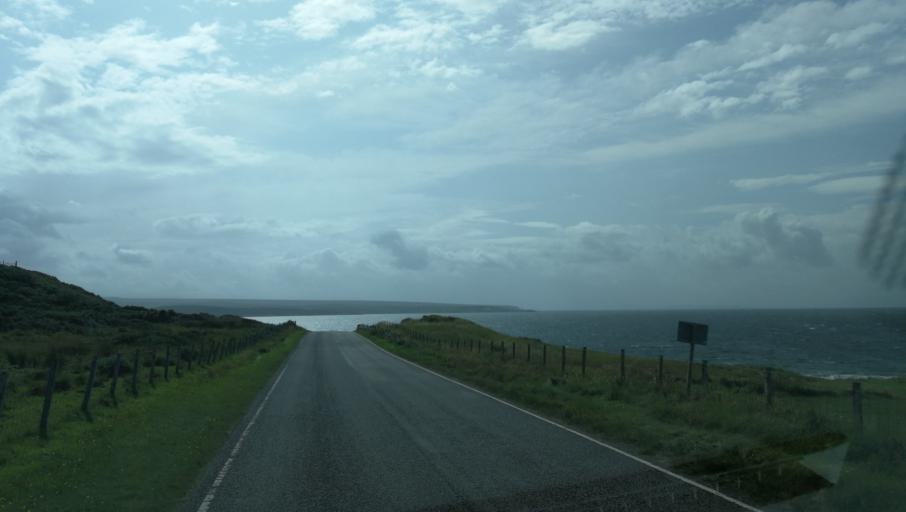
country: GB
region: Scotland
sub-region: Highland
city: Portree
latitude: 57.7362
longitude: -5.7634
